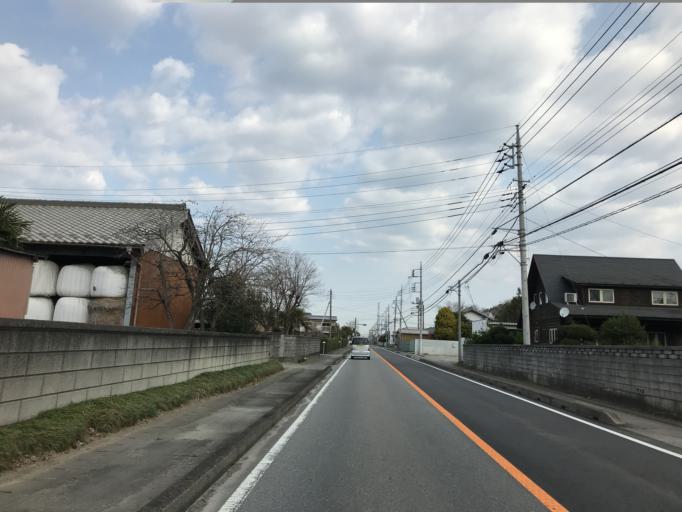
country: JP
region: Ibaraki
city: Mitsukaido
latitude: 36.0095
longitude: 140.0123
